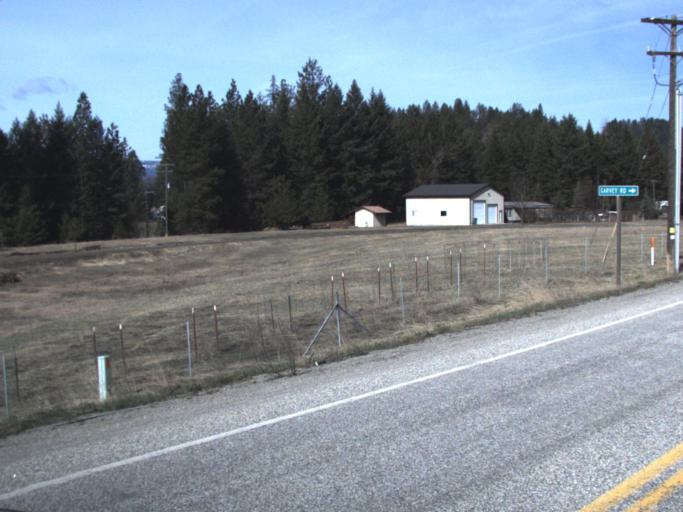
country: US
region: Washington
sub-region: Stevens County
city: Colville
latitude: 48.5234
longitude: -117.8153
